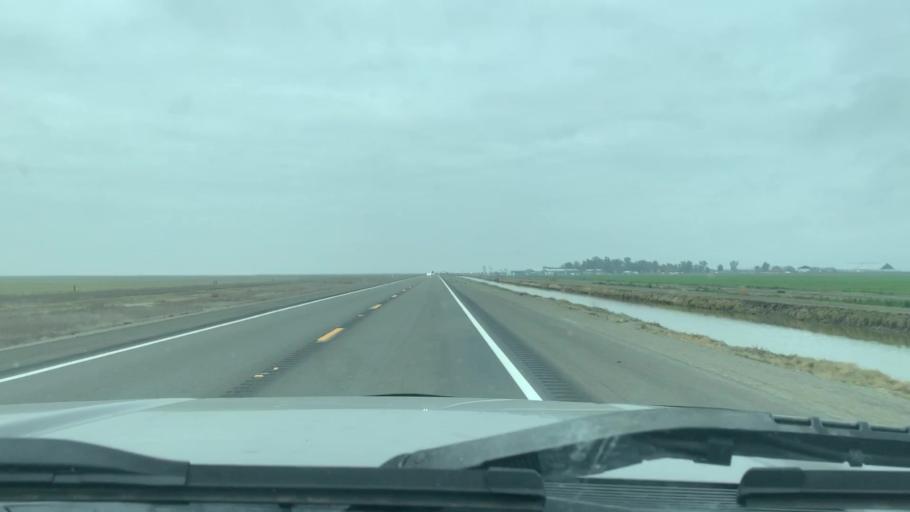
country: US
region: California
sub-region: Kings County
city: Stratford
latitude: 36.1131
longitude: -119.8986
